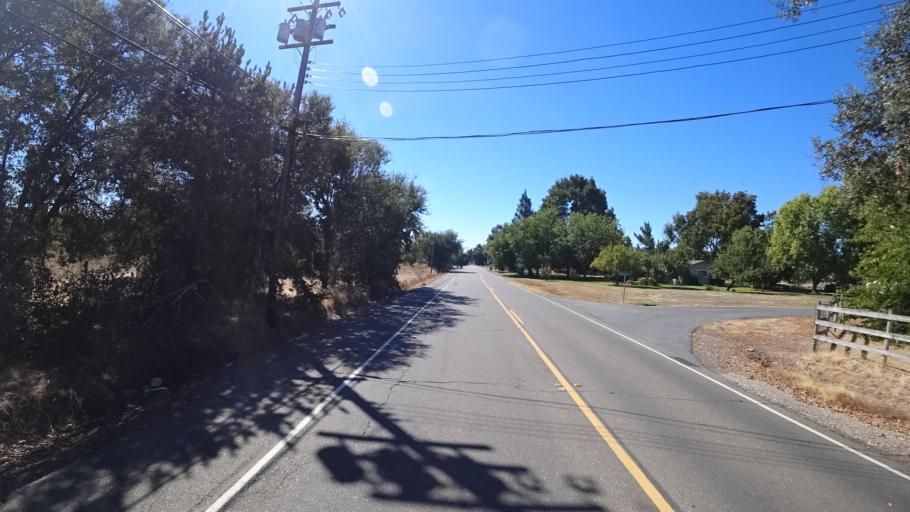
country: US
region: California
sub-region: Sacramento County
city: Vineyard
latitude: 38.4300
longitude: -121.3252
